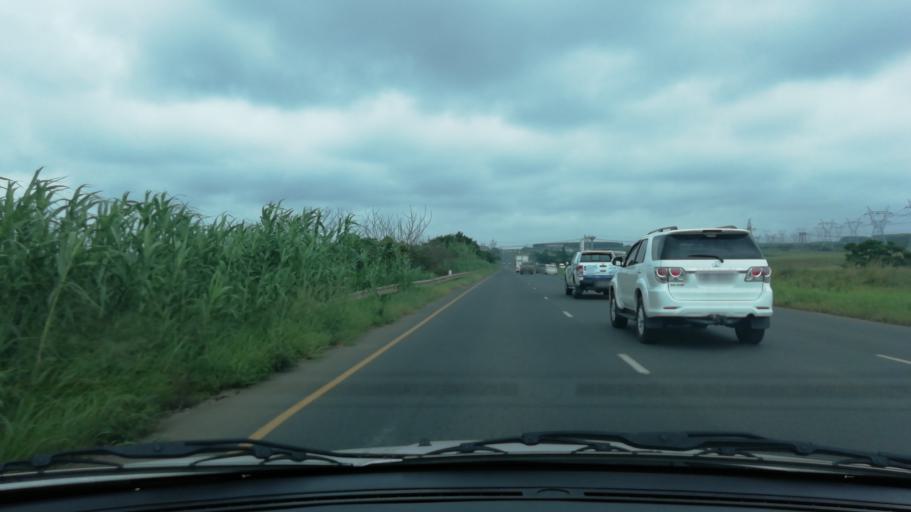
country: ZA
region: KwaZulu-Natal
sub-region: uThungulu District Municipality
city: Empangeni
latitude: -28.7729
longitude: 31.9473
